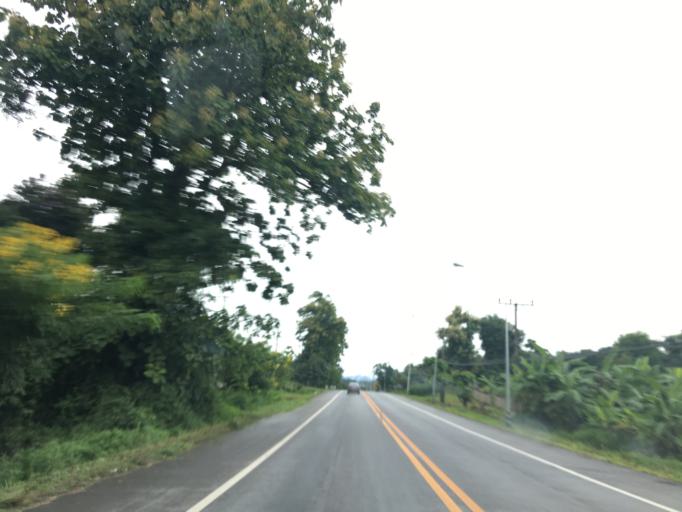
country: TH
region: Chiang Rai
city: Pa Daet
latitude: 19.6838
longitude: 99.9248
